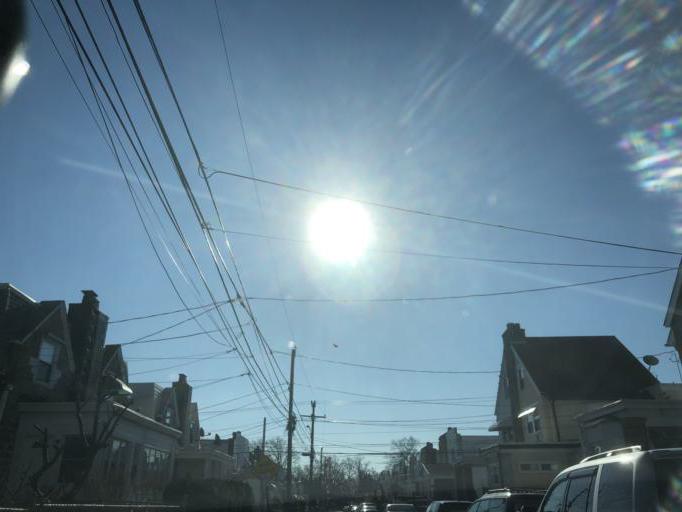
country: US
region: Pennsylvania
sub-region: Delaware County
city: Millbourne
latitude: 39.9589
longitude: -75.2540
